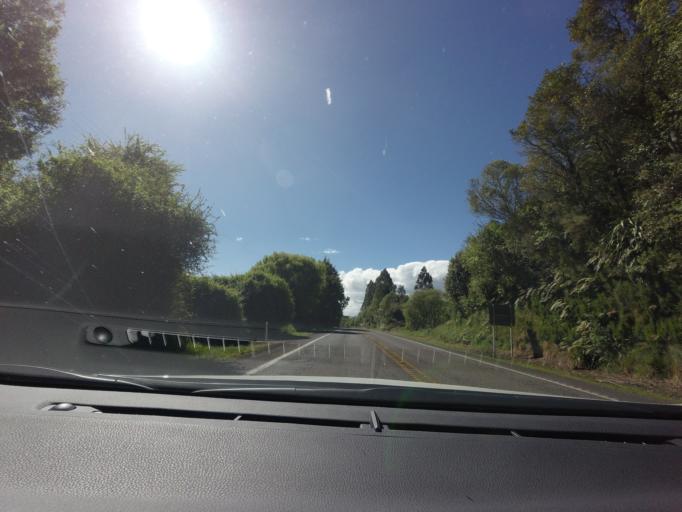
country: NZ
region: Bay of Plenty
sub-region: Rotorua District
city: Rotorua
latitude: -38.0802
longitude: 176.1856
